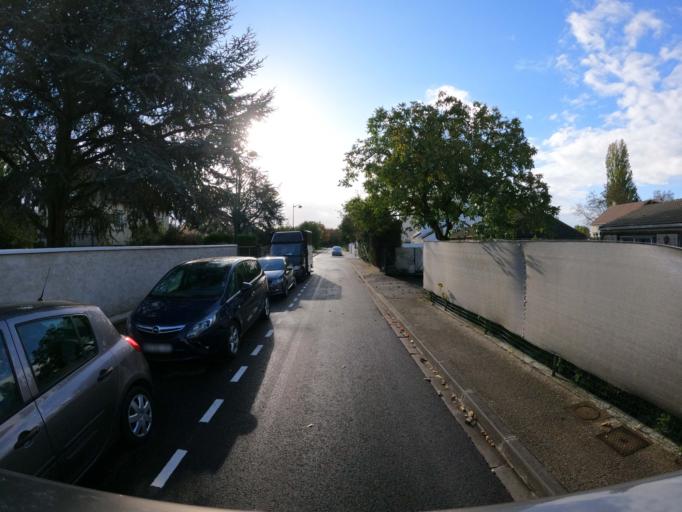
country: FR
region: Ile-de-France
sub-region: Departement de Seine-et-Marne
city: Bailly-Romainvilliers
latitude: 48.8460
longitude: 2.8226
